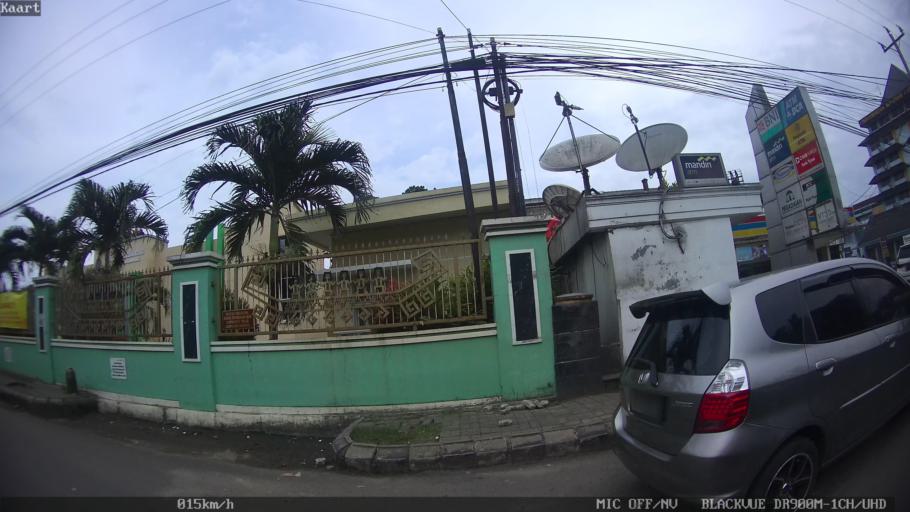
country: ID
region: Lampung
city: Kedaton
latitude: -5.3795
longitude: 105.2530
